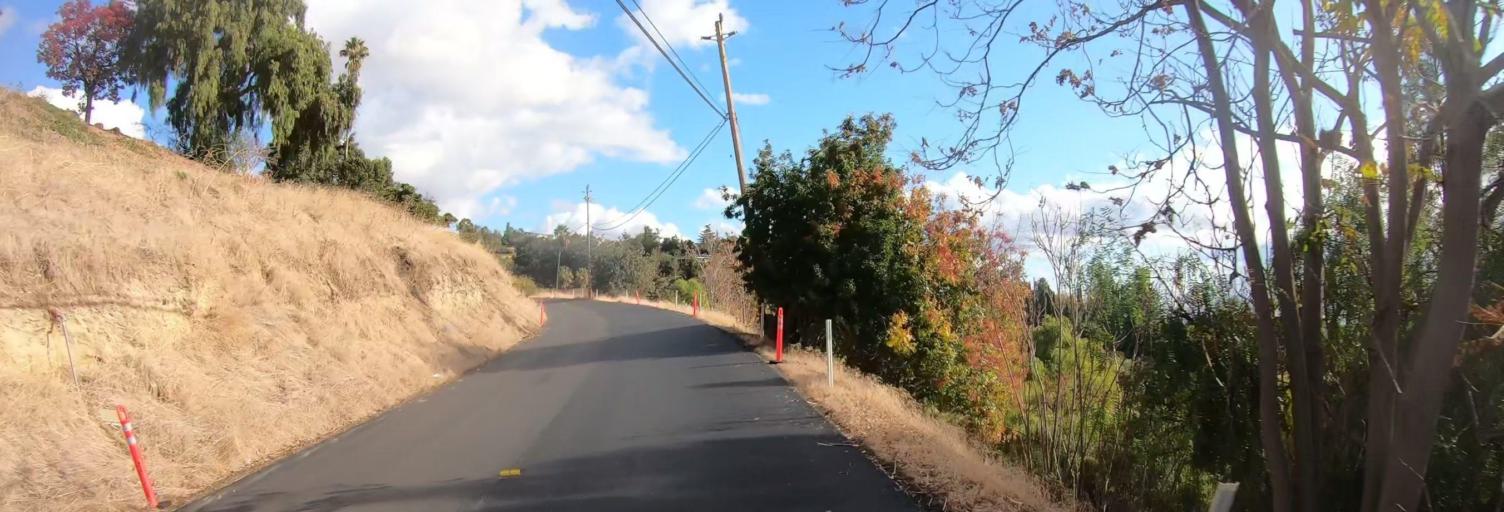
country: US
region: California
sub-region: Santa Clara County
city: East Foothills
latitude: 37.3772
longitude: -121.8047
